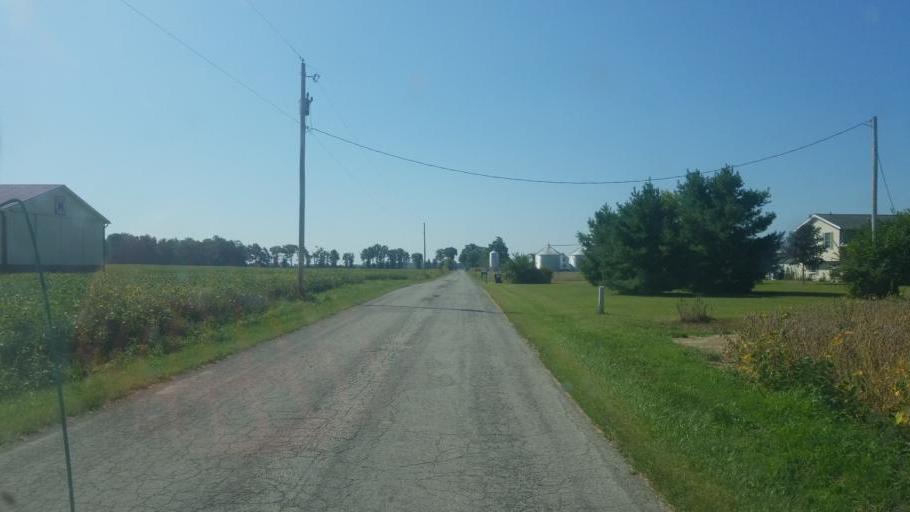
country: US
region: Ohio
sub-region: Morrow County
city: Cardington
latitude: 40.5857
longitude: -82.9382
